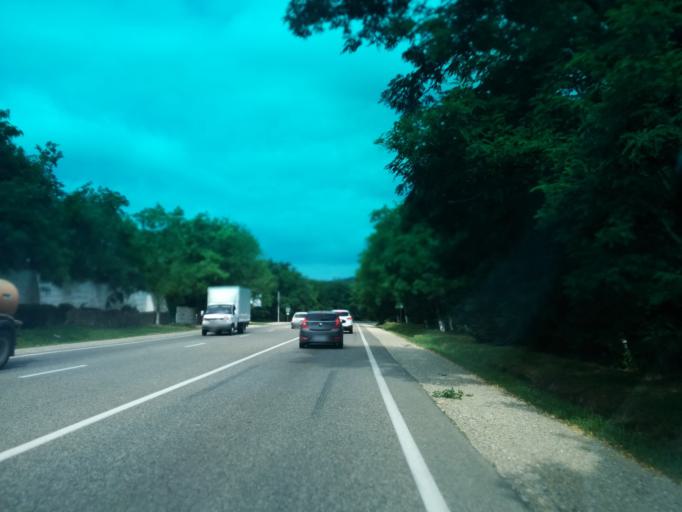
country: RU
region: Krasnodarskiy
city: Nebug
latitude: 44.1707
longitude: 38.9792
